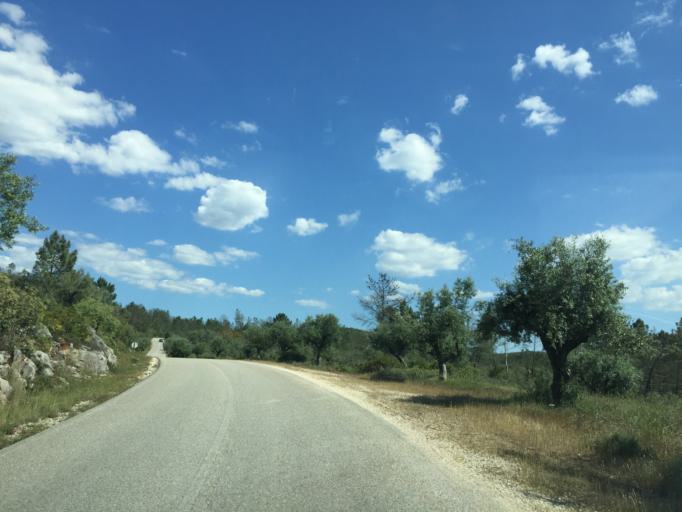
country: PT
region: Leiria
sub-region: Alvaiazere
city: Alvaiazere
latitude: 39.8086
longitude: -8.4252
